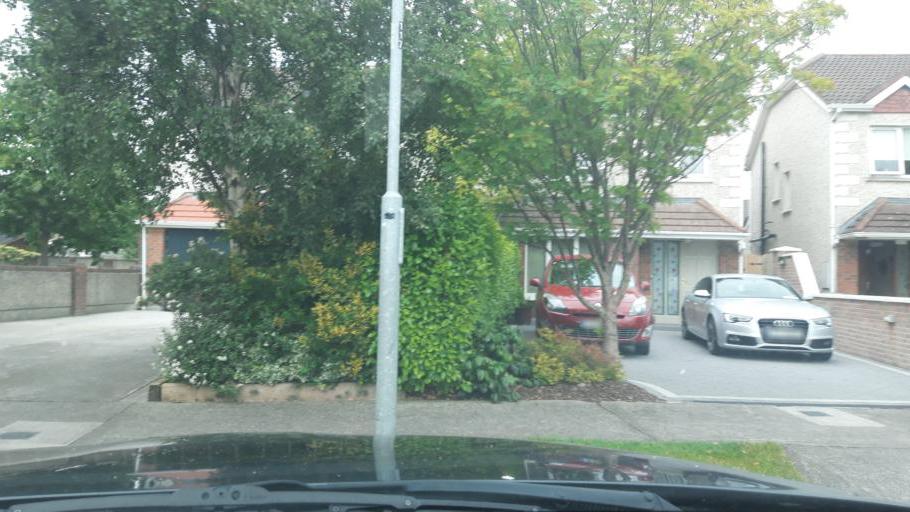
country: IE
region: Leinster
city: Hartstown
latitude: 53.4037
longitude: -6.4161
